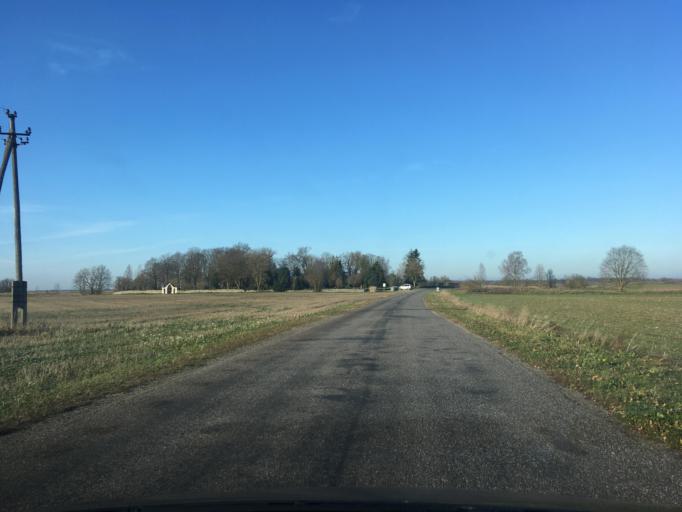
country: EE
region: Harju
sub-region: Raasiku vald
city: Arukula
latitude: 59.4479
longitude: 25.1195
